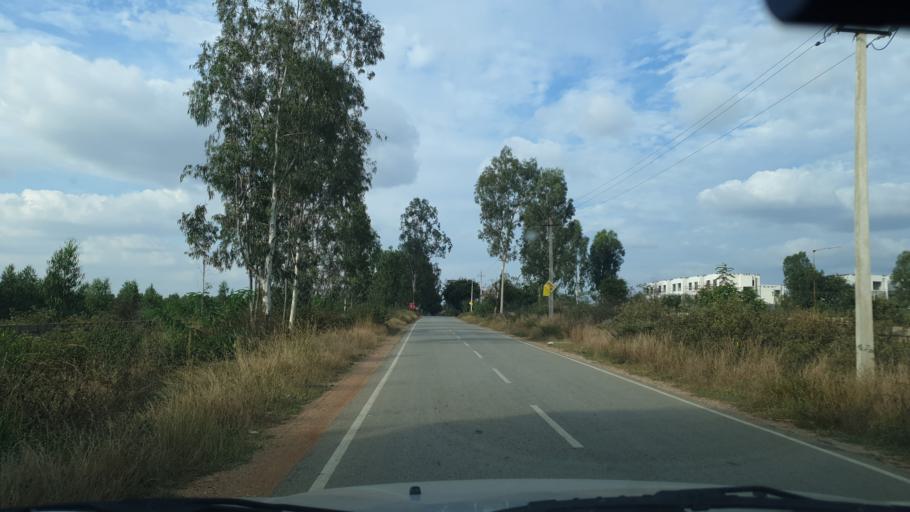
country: IN
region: Karnataka
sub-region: Bangalore Urban
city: Yelahanka
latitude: 13.2013
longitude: 77.6029
